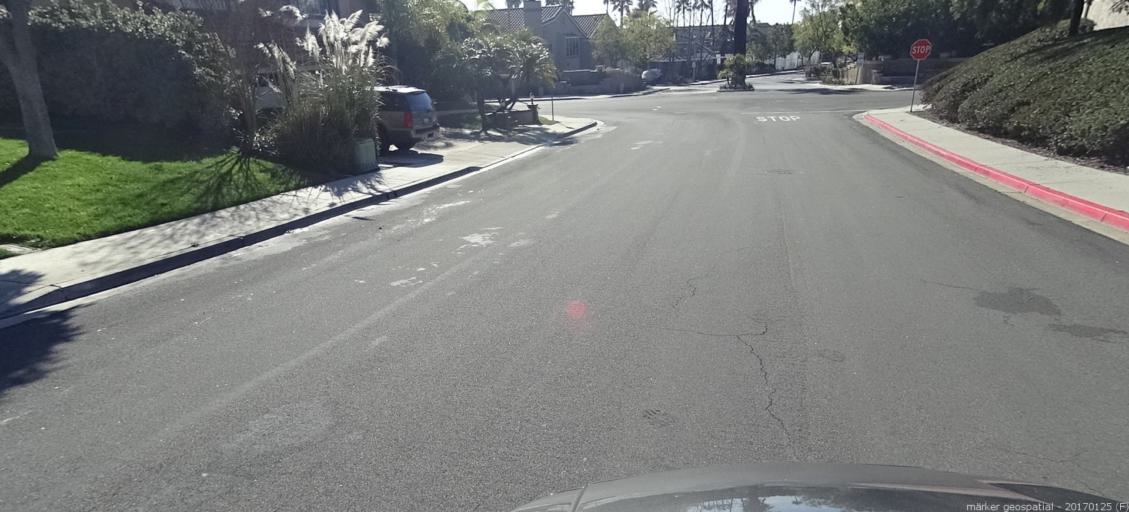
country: US
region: California
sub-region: Orange County
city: Portola Hills
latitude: 33.6814
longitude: -117.6349
